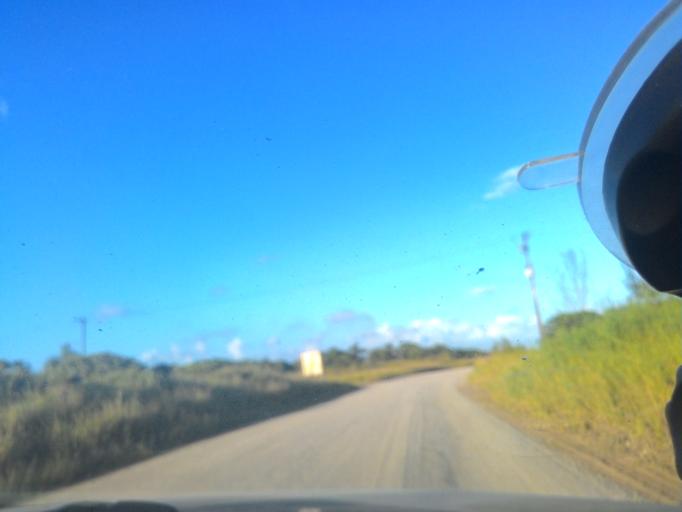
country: BR
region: Sao Paulo
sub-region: Pariquera-Acu
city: Pariquera Acu
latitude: -24.8655
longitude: -47.7168
